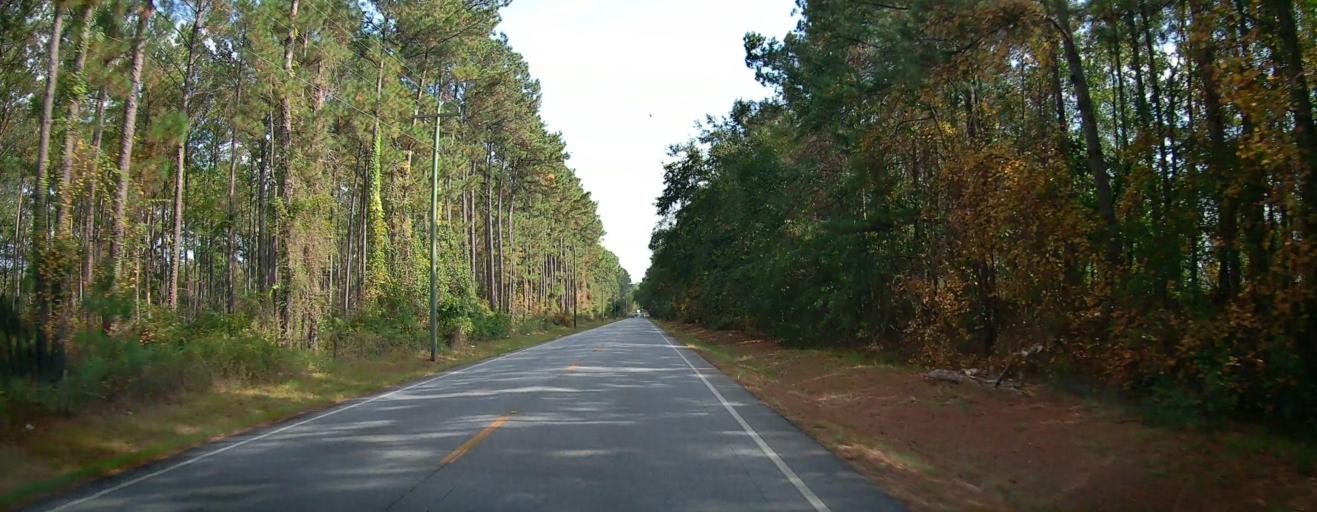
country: US
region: Georgia
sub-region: Thomas County
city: Thomasville
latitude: 30.9274
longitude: -84.0190
